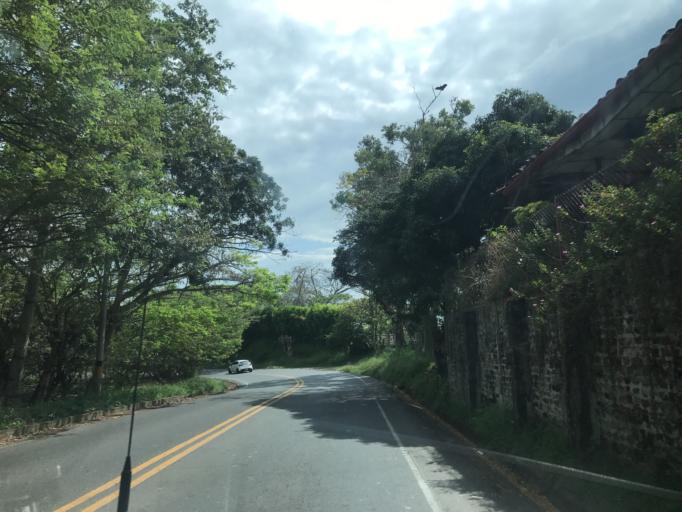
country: CO
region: Valle del Cauca
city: Cartago
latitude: 4.7271
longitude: -75.8902
